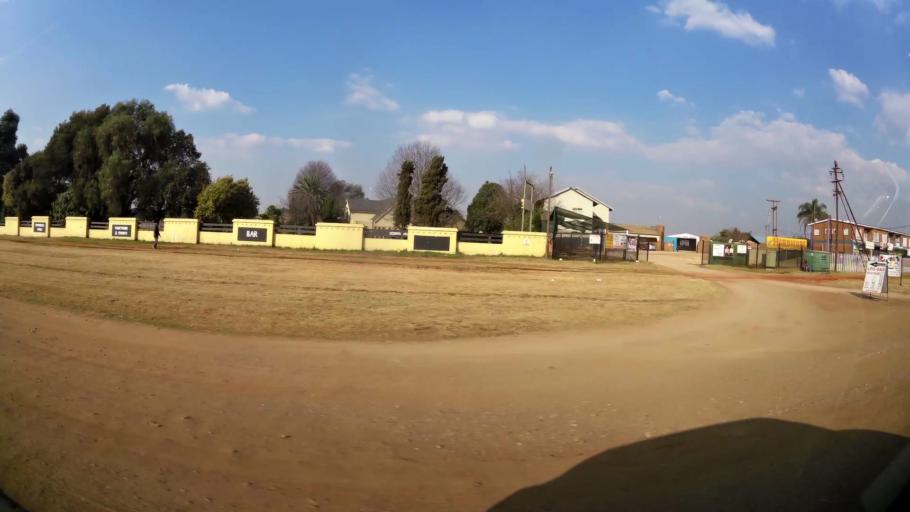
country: ZA
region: Gauteng
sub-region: Ekurhuleni Metropolitan Municipality
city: Benoni
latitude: -26.1081
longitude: 28.2960
